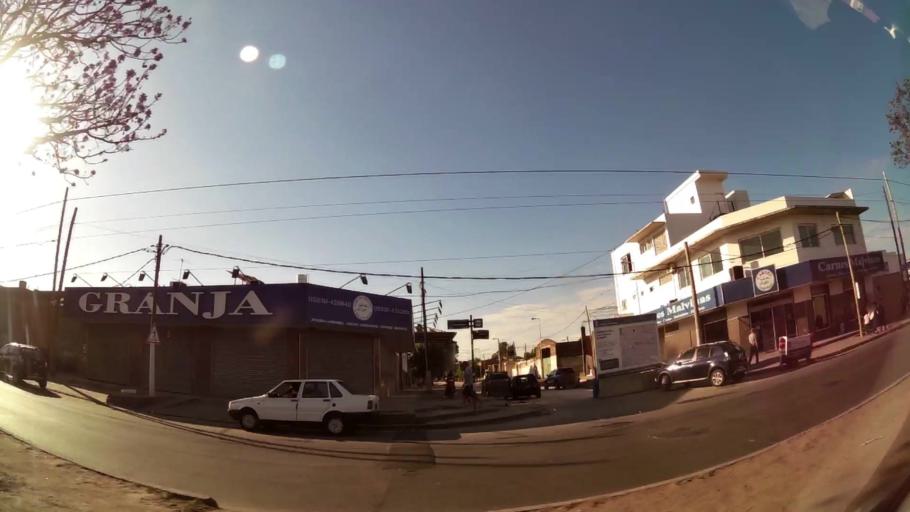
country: AR
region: Buenos Aires
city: Hurlingham
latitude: -34.5051
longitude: -58.7194
